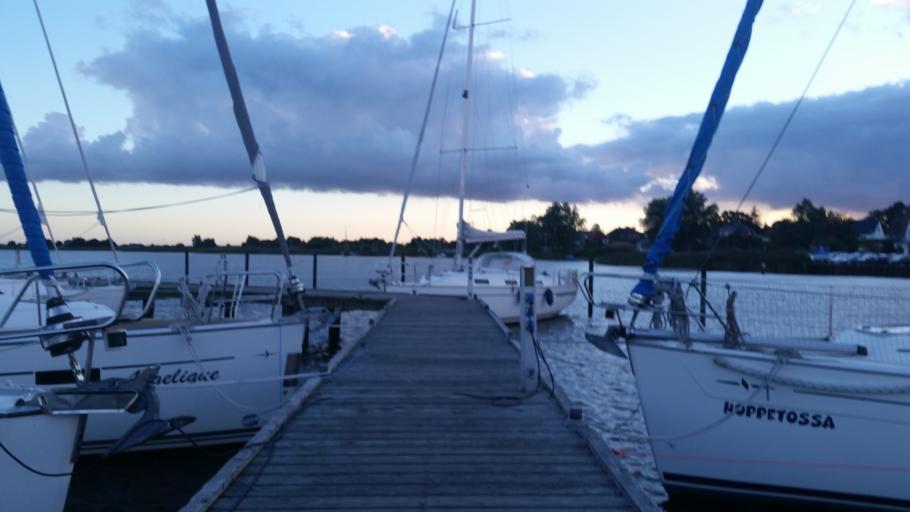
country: DE
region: Mecklenburg-Vorpommern
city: Altenkirchen
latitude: 54.6119
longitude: 13.3568
